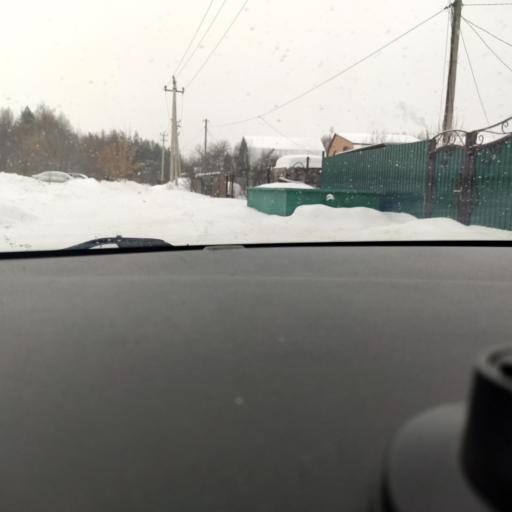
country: RU
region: Bashkortostan
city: Avdon
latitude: 54.6785
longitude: 55.7908
